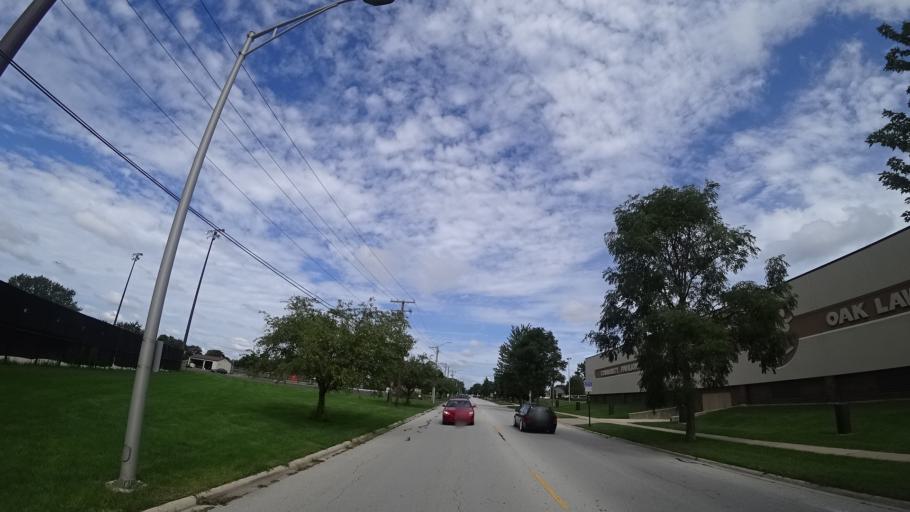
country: US
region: Illinois
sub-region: Cook County
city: Burbank
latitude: 41.7215
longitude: -87.7898
